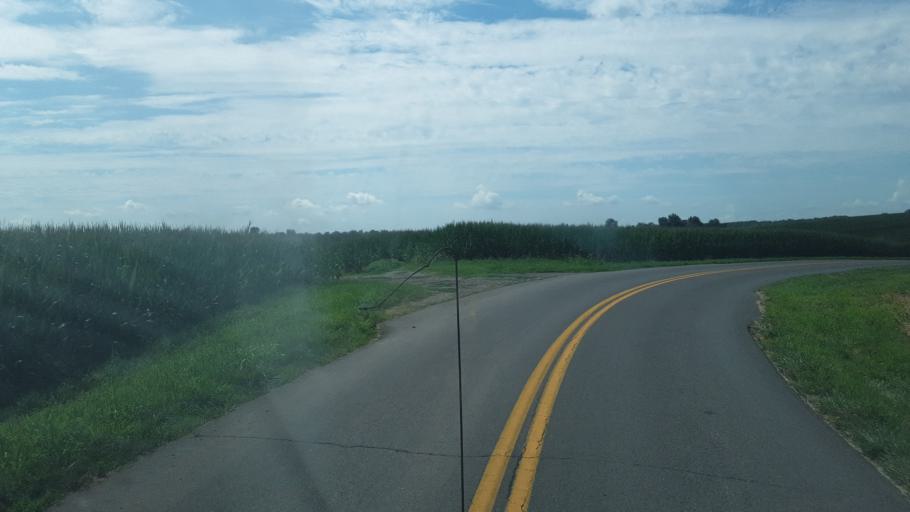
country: US
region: Kentucky
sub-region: Christian County
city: Oak Grove
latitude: 36.7449
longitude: -87.3166
